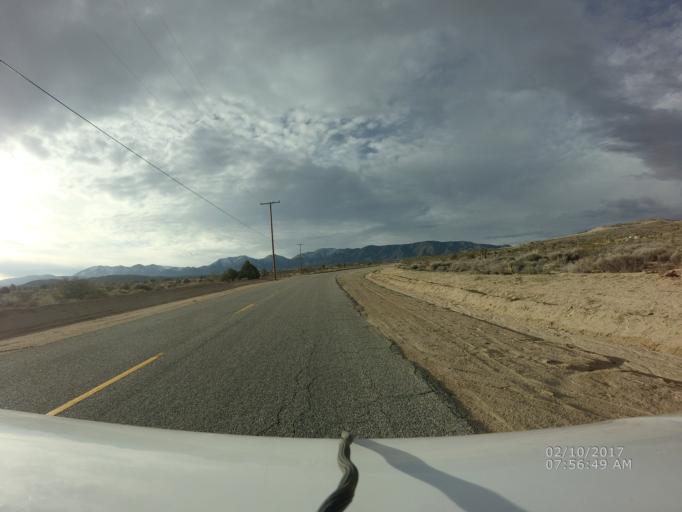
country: US
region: California
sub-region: Los Angeles County
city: Littlerock
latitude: 34.4981
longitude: -117.9055
